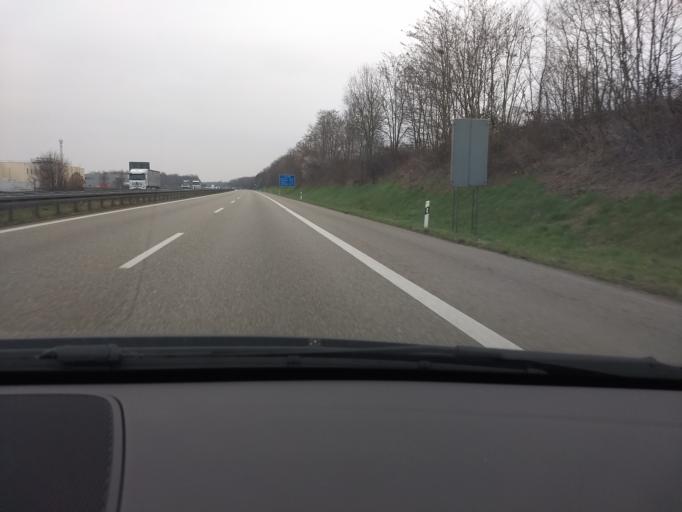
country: DE
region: Baden-Wuerttemberg
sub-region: Freiburg Region
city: Neuenburg am Rhein
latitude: 47.8201
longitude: 7.5575
